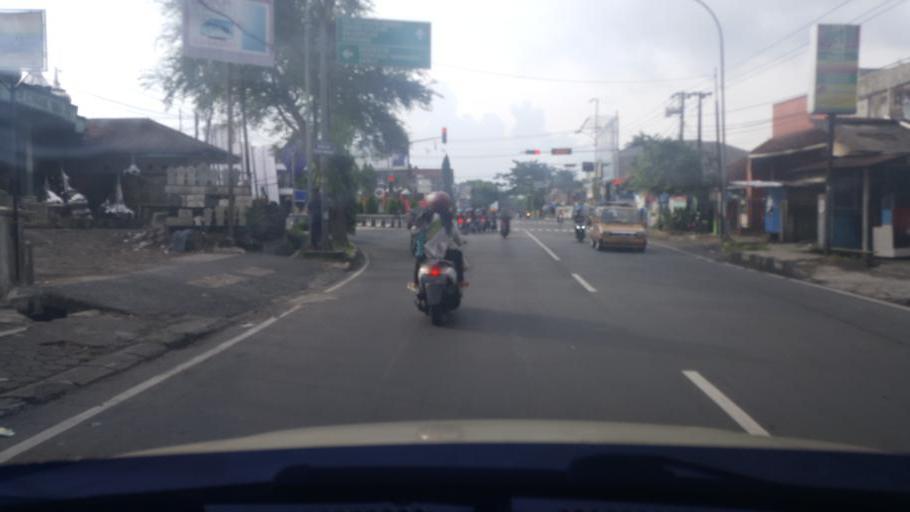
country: ID
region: West Java
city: Jati
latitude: -7.3047
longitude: 108.2059
